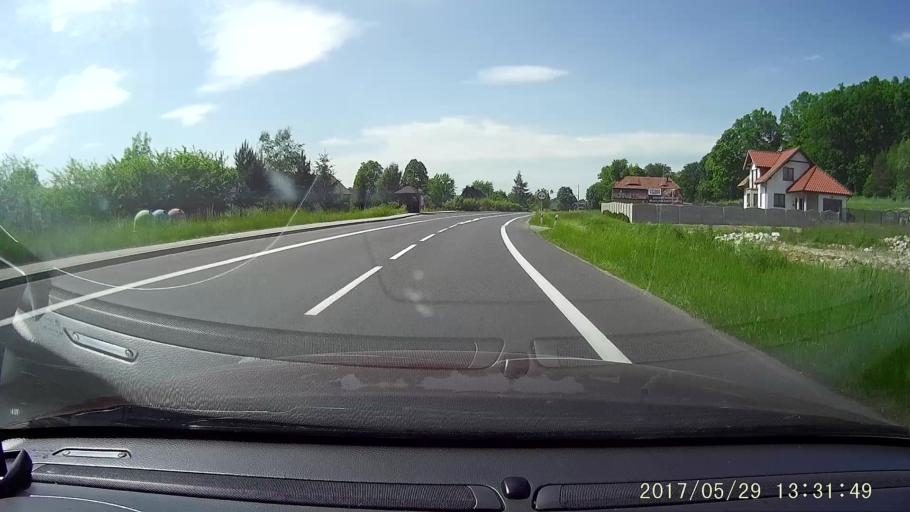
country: PL
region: Lower Silesian Voivodeship
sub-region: Powiat lubanski
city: Olszyna
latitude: 51.0813
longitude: 15.3351
